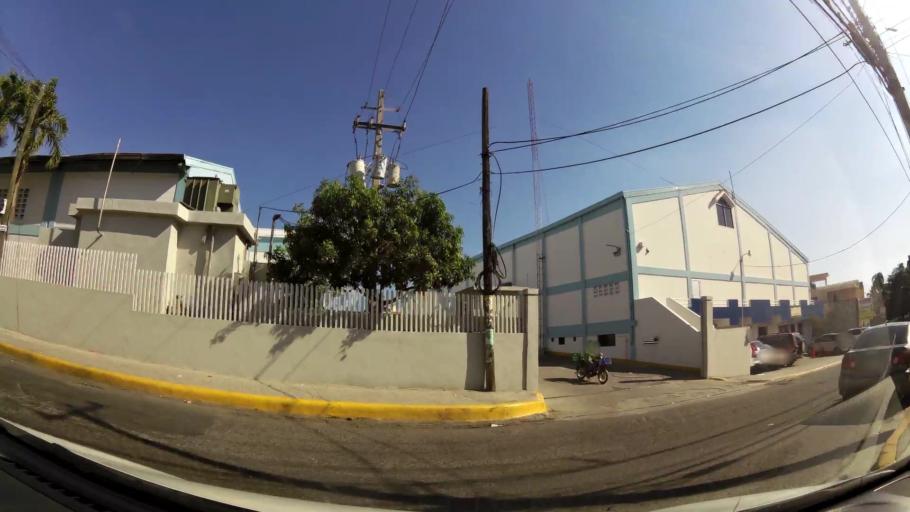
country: DO
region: Nacional
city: Santo Domingo
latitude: 18.4729
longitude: -69.9918
